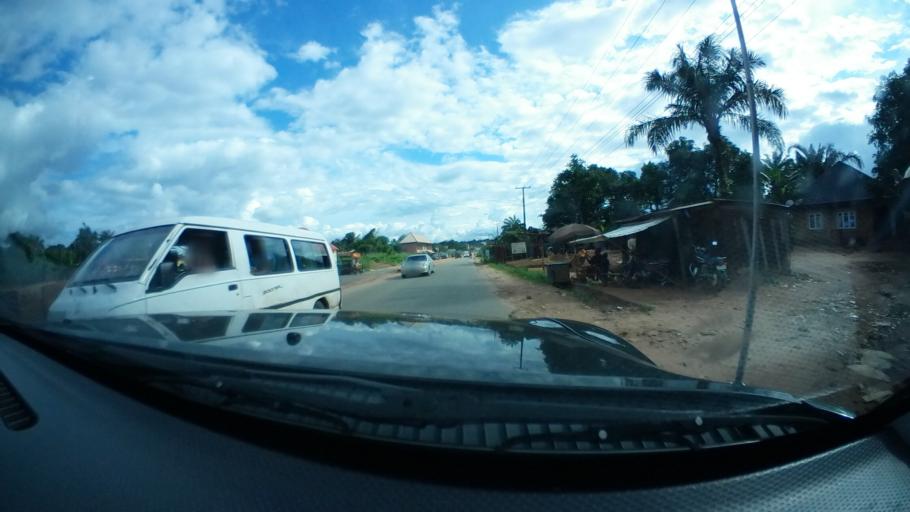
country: NG
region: Anambra
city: Uga
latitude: 5.9044
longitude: 7.1092
